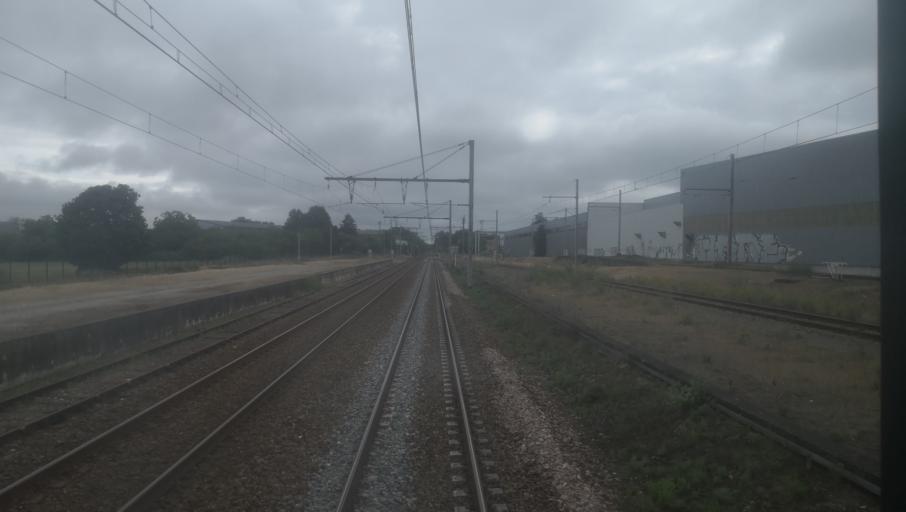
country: FR
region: Centre
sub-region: Departement de l'Indre
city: Chateauroux
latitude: 46.8173
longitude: 1.7186
